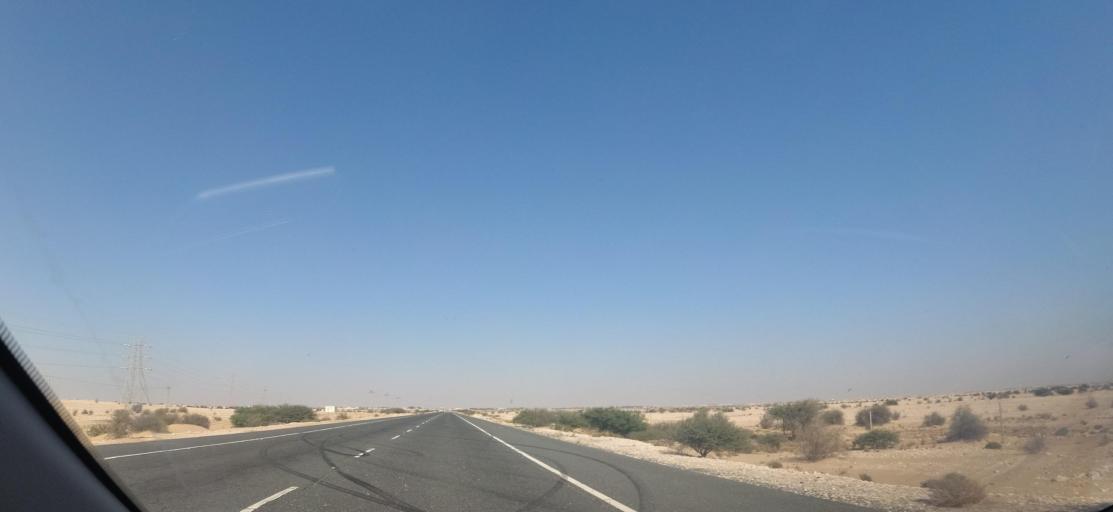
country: QA
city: Al Jumayliyah
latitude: 25.5935
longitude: 51.0664
